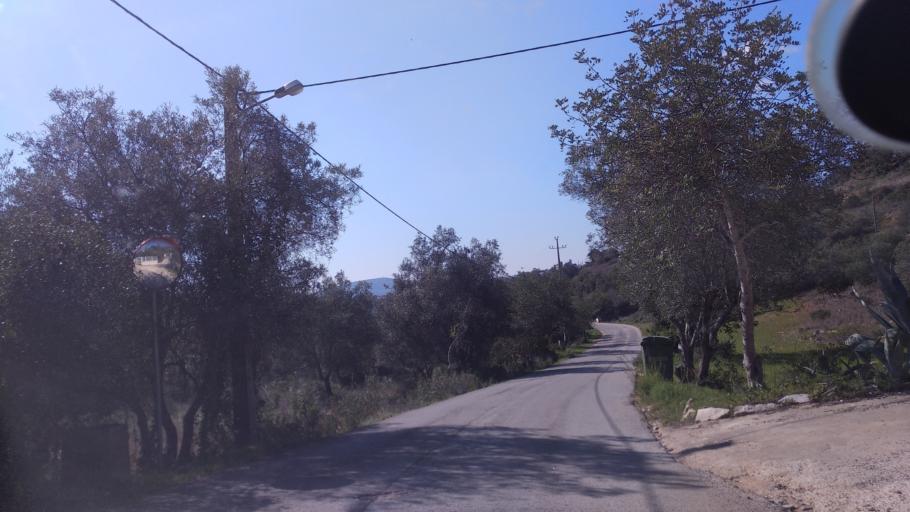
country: PT
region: Faro
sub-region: Sao Bras de Alportel
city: Sao Bras de Alportel
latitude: 37.1357
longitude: -7.9104
